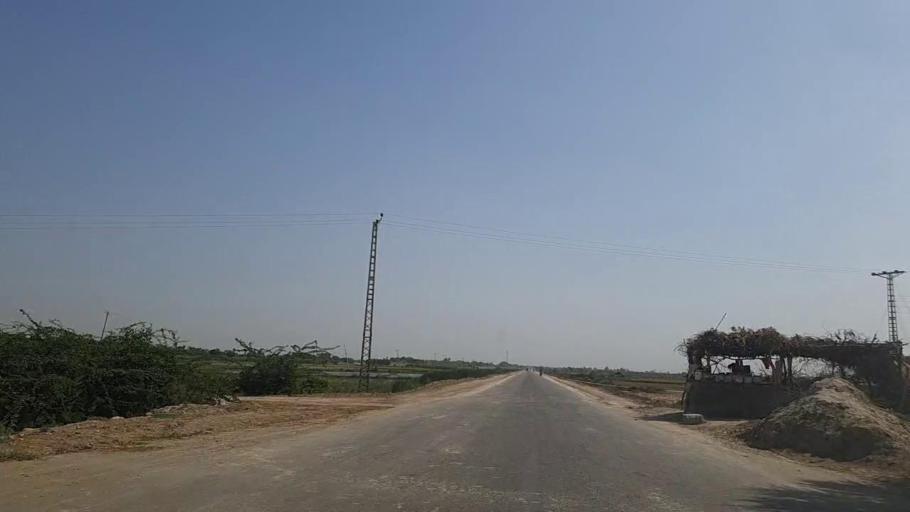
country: PK
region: Sindh
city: Mirpur Batoro
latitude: 24.7501
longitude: 68.2361
